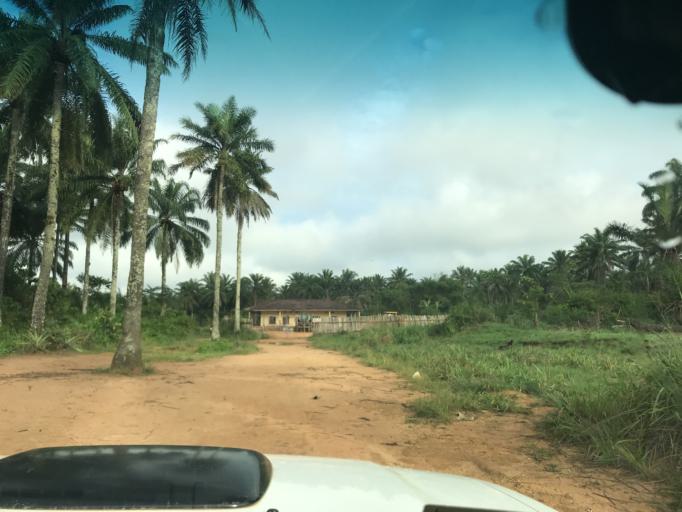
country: CD
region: Eastern Province
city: Kisangani
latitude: 0.9970
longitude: 25.2388
